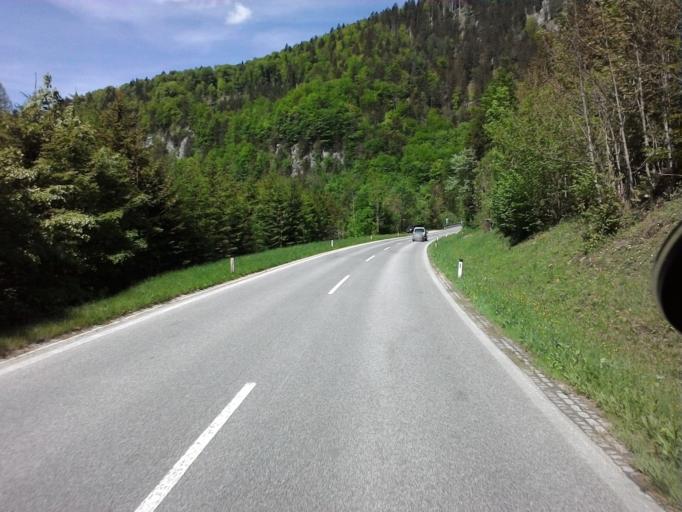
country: AT
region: Styria
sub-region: Politischer Bezirk Liezen
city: Palfau
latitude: 47.7118
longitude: 14.8339
